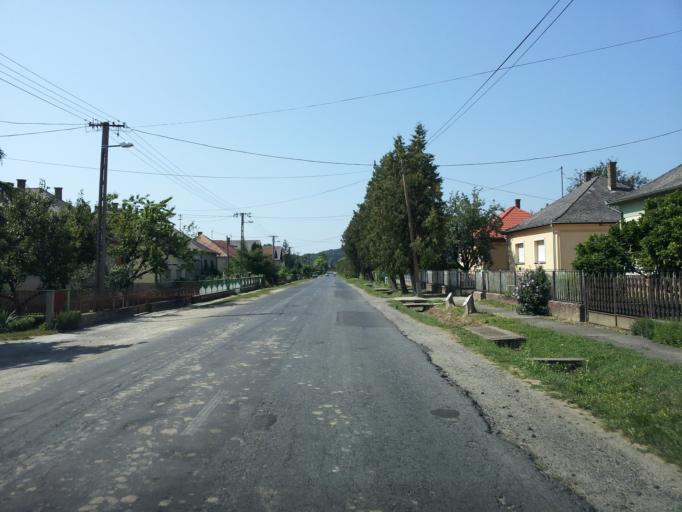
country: HU
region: Zala
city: Heviz
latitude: 46.8416
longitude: 17.0947
